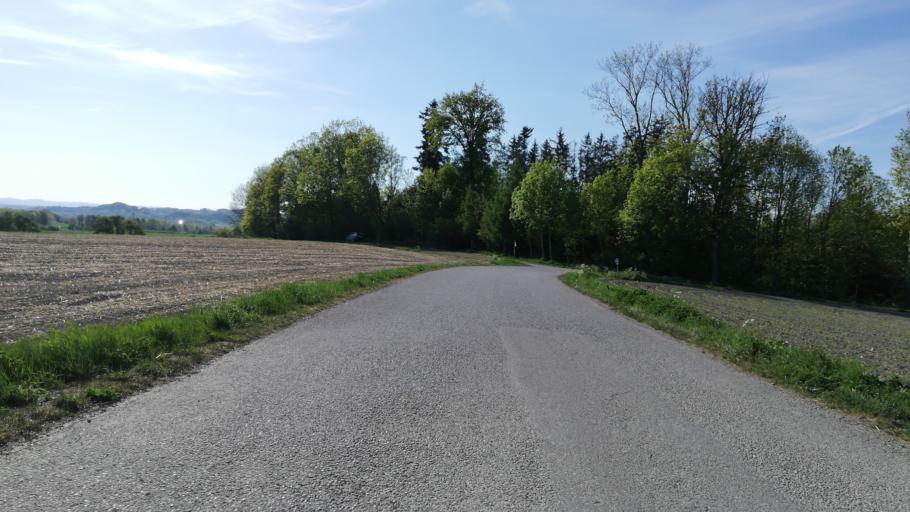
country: AT
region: Upper Austria
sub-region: Politischer Bezirk Grieskirchen
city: Bad Schallerbach
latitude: 48.1905
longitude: 13.9426
